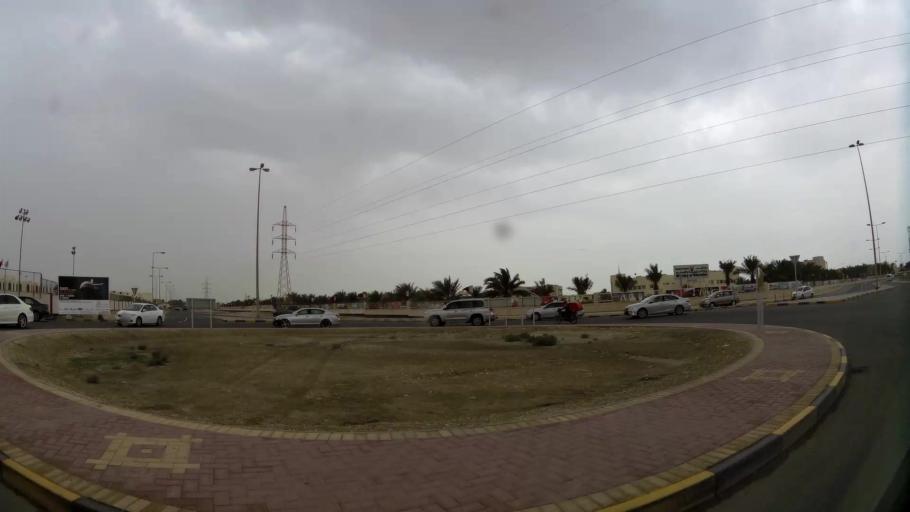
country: BH
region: Northern
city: Madinat `Isa
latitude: 26.1621
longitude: 50.5512
